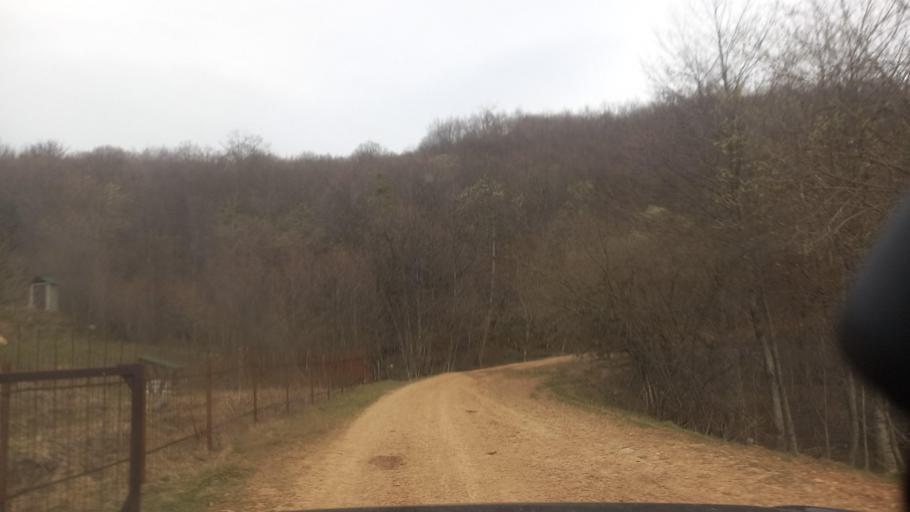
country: RU
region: Adygeya
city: Kamennomostskiy
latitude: 44.2109
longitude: 40.0263
